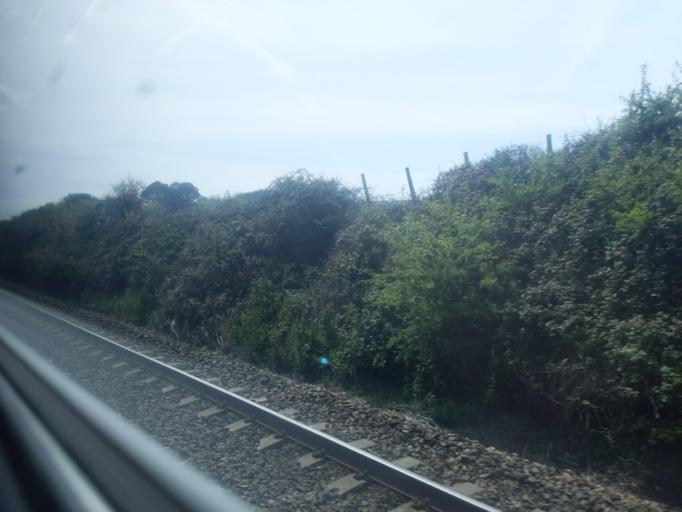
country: GB
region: England
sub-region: Cornwall
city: Marazion
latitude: 50.1396
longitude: -5.4688
